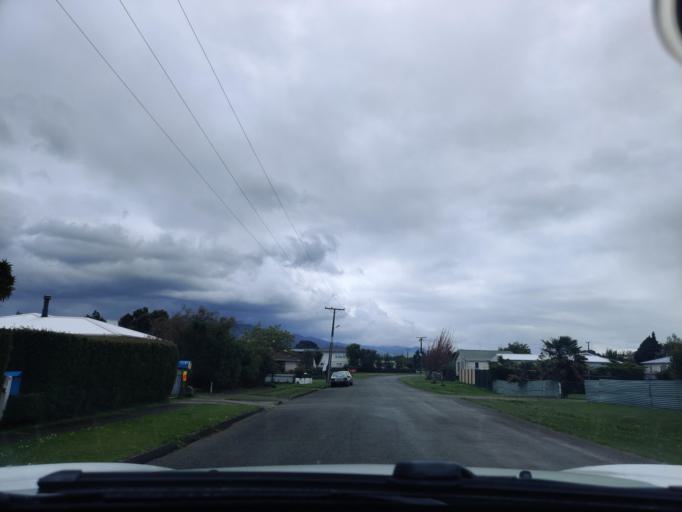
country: NZ
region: Manawatu-Wanganui
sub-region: Palmerston North City
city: Palmerston North
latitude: -40.3354
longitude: 175.8643
